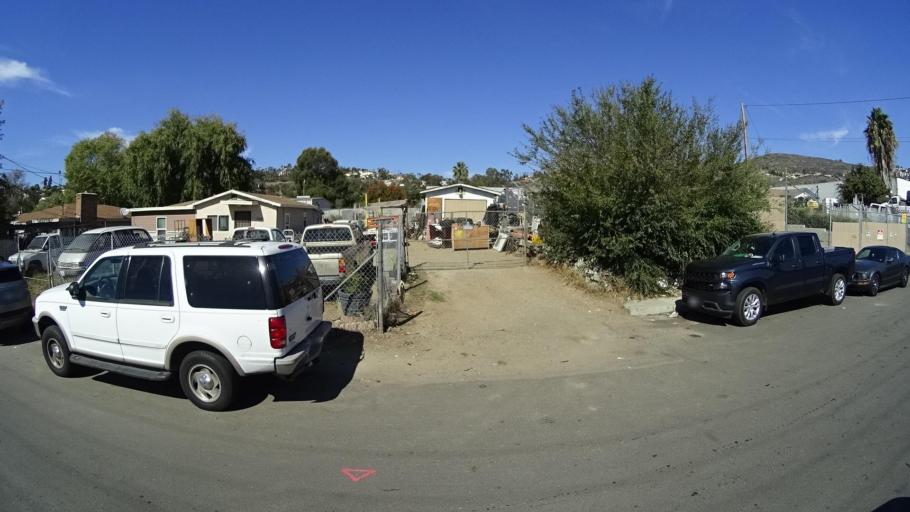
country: US
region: California
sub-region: San Diego County
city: La Presa
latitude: 32.7166
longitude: -117.0049
